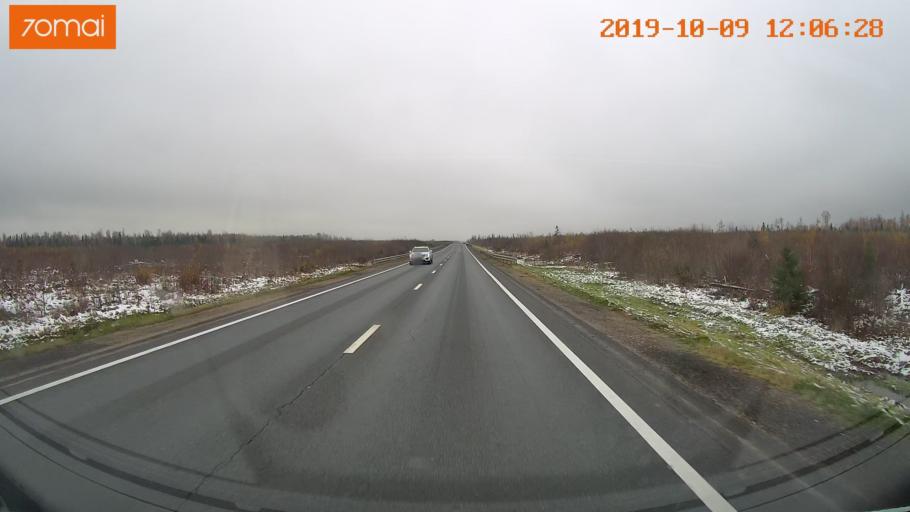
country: RU
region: Jaroslavl
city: Prechistoye
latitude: 58.6139
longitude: 40.3354
